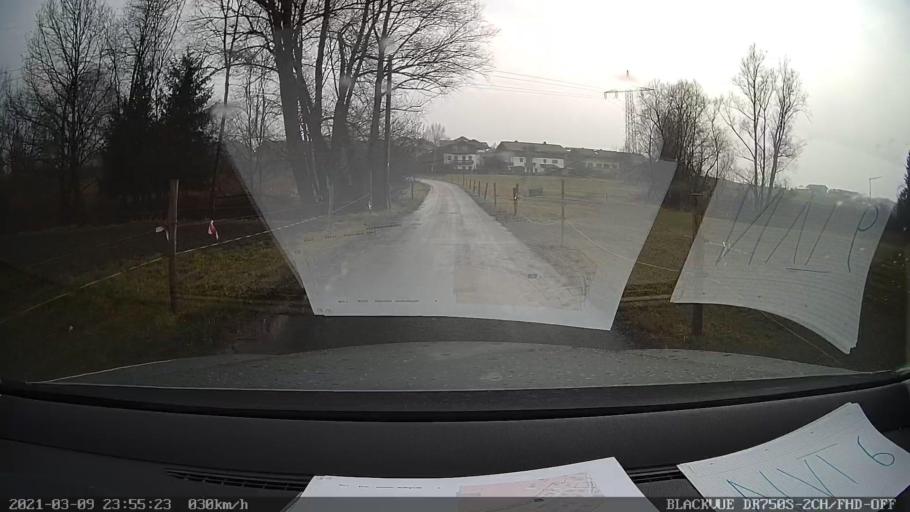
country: DE
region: Bavaria
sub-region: Upper Bavaria
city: Schonstett
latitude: 47.9824
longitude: 12.2366
